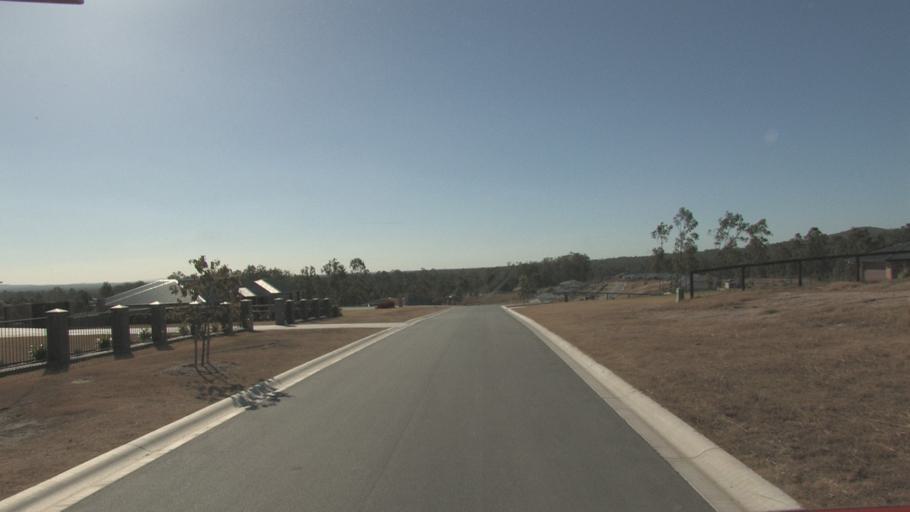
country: AU
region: Queensland
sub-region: Logan
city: Cedar Vale
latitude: -27.8721
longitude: 153.0520
